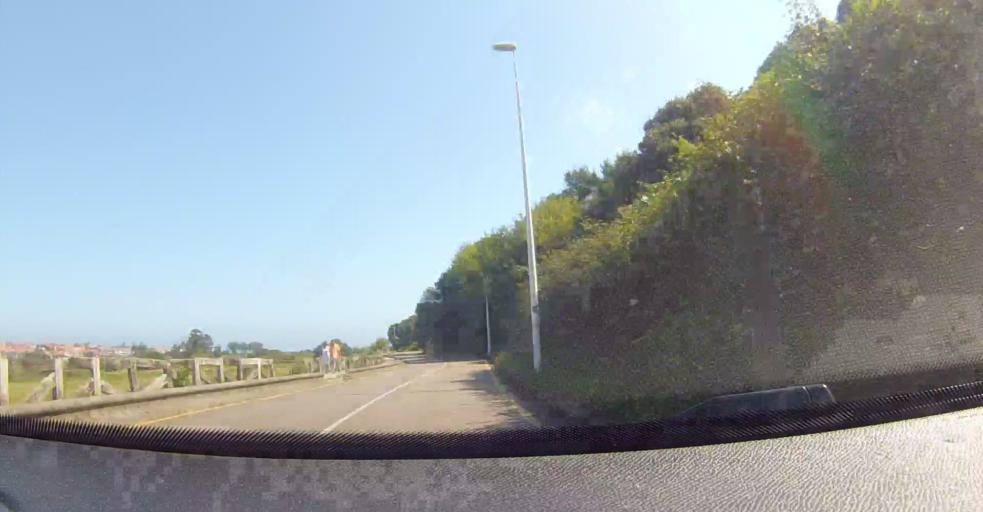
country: ES
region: Cantabria
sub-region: Provincia de Cantabria
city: Noja
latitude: 43.4668
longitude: -3.5181
